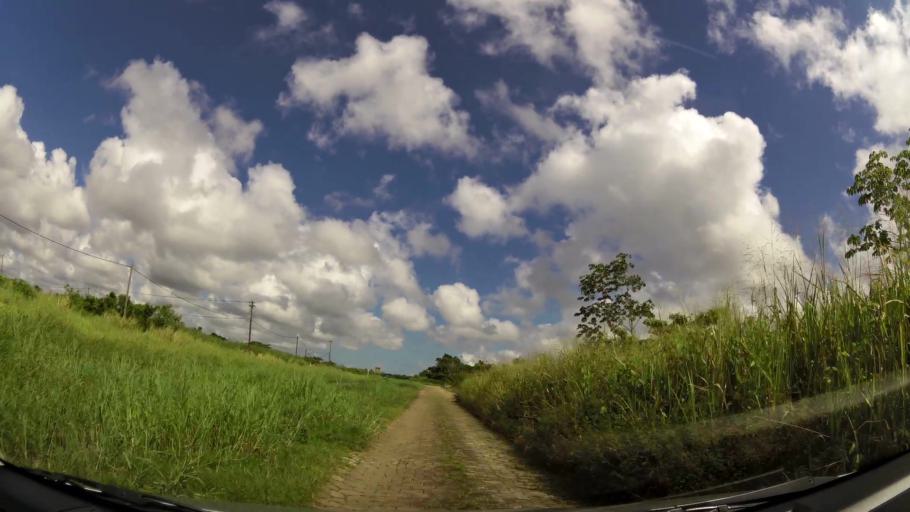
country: SR
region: Paramaribo
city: Paramaribo
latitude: 5.8700
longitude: -55.1263
